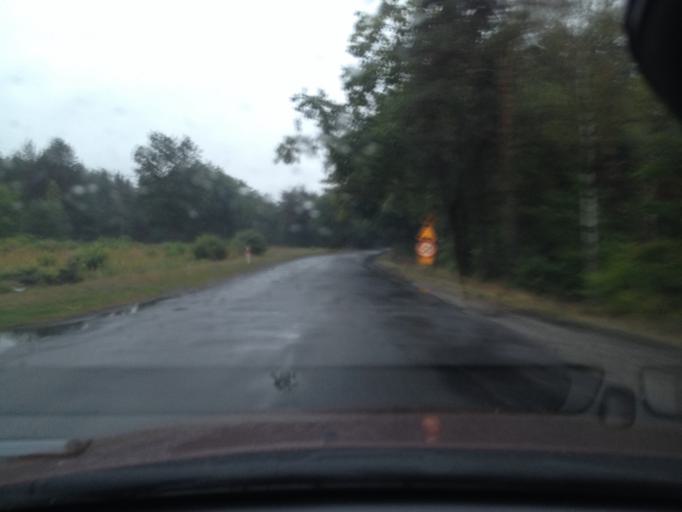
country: PL
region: Lubusz
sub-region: Powiat zaganski
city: Gozdnica
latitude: 51.3818
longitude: 15.1733
